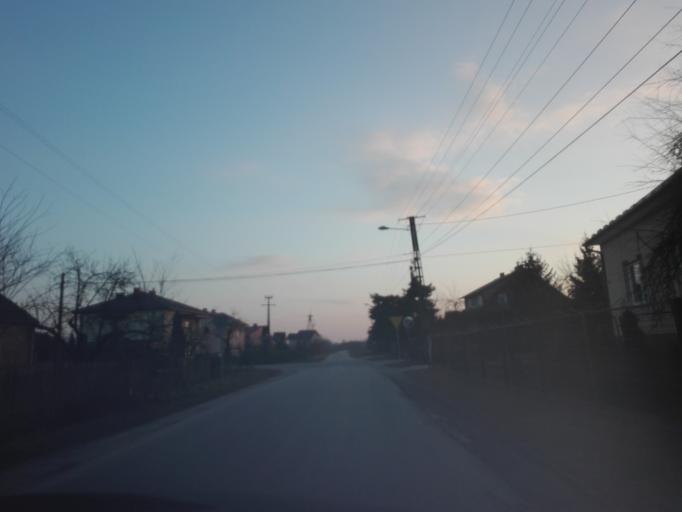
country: PL
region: Subcarpathian Voivodeship
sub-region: Powiat tarnobrzeski
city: Sokolniki
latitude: 50.6428
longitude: 21.8017
